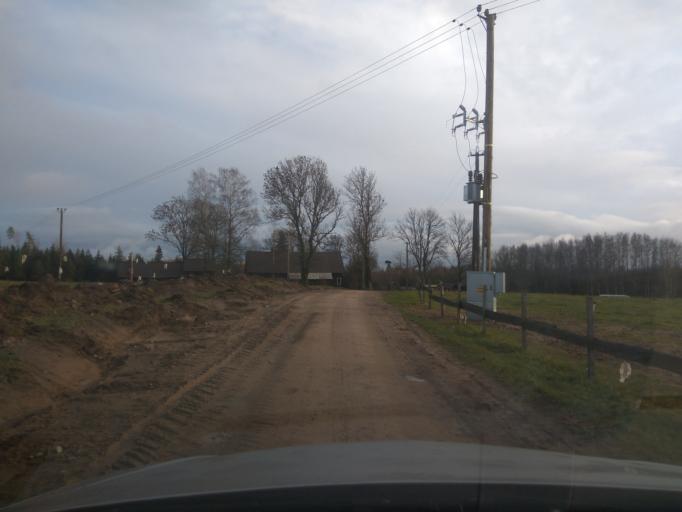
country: LV
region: Kuldigas Rajons
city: Kuldiga
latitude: 56.8303
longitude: 21.8286
